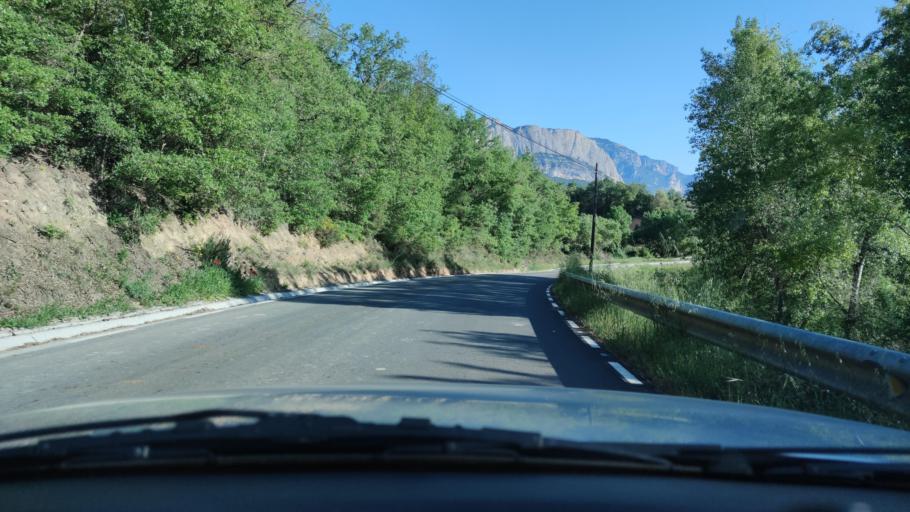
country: ES
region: Catalonia
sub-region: Provincia de Lleida
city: Oliana
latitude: 42.0485
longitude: 1.2927
